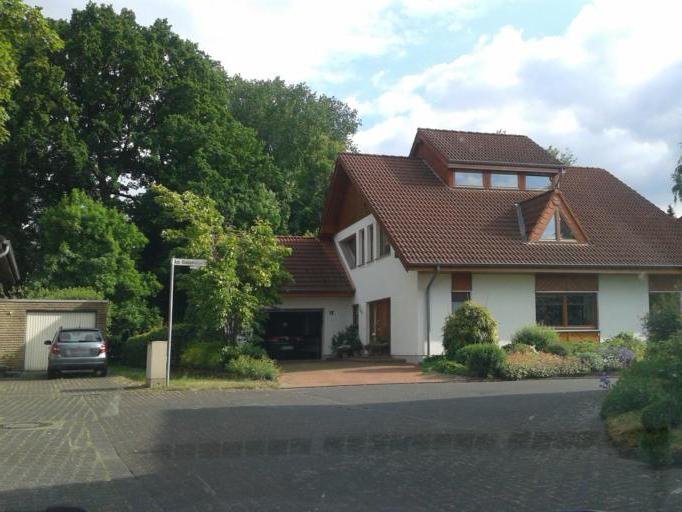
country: DE
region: North Rhine-Westphalia
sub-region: Regierungsbezirk Detmold
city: Paderborn
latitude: 51.7418
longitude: 8.6857
